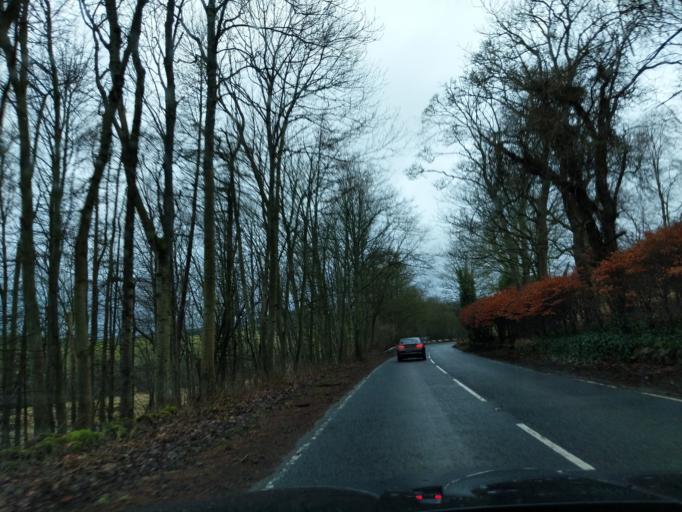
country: GB
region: Scotland
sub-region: The Scottish Borders
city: Galashiels
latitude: 55.6446
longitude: -2.8528
